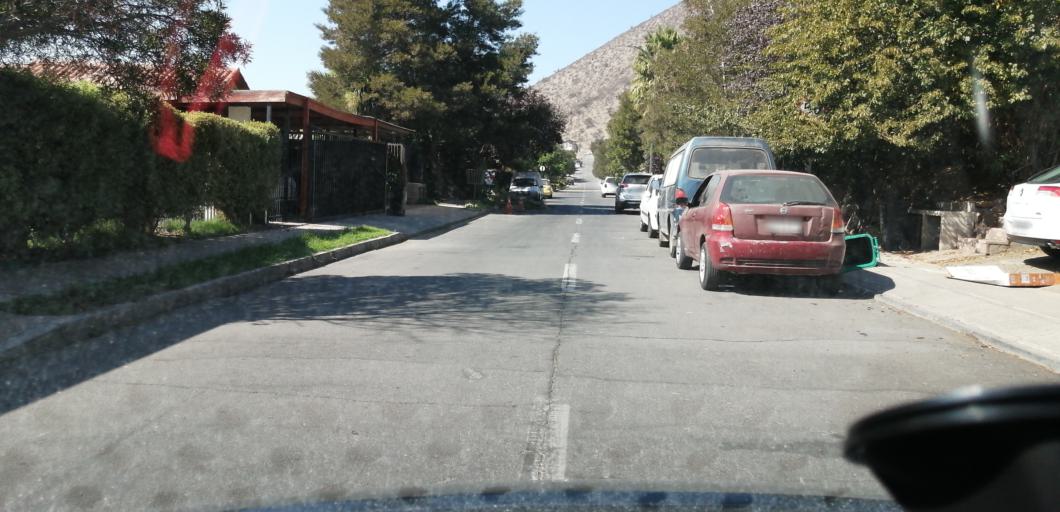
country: CL
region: Santiago Metropolitan
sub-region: Provincia de Santiago
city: Lo Prado
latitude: -33.4565
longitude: -70.8259
